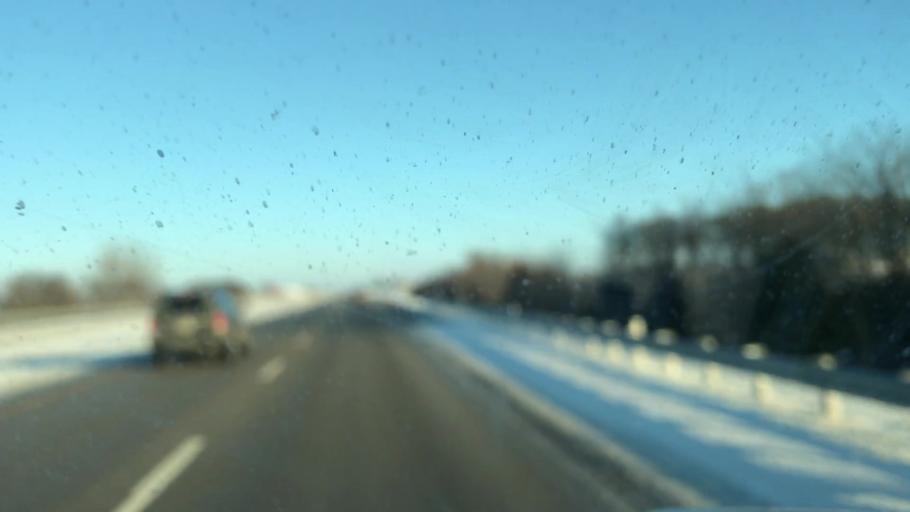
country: US
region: Missouri
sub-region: Buchanan County
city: Saint Joseph
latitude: 39.7477
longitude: -94.7014
